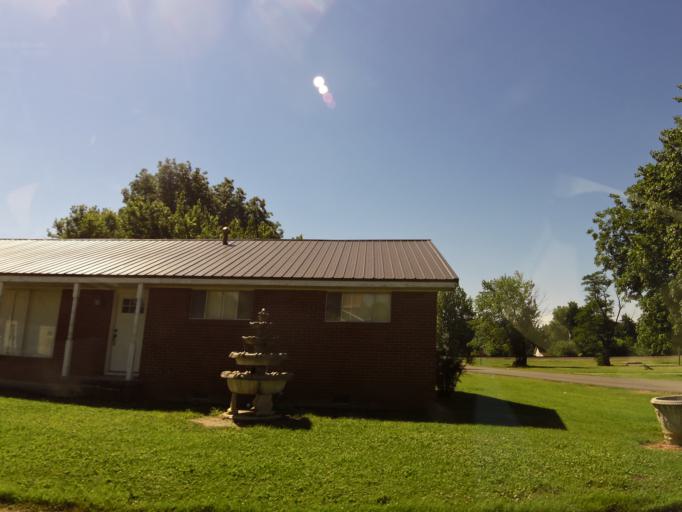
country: US
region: Missouri
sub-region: Dunklin County
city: Campbell
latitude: 36.4947
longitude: -90.0723
